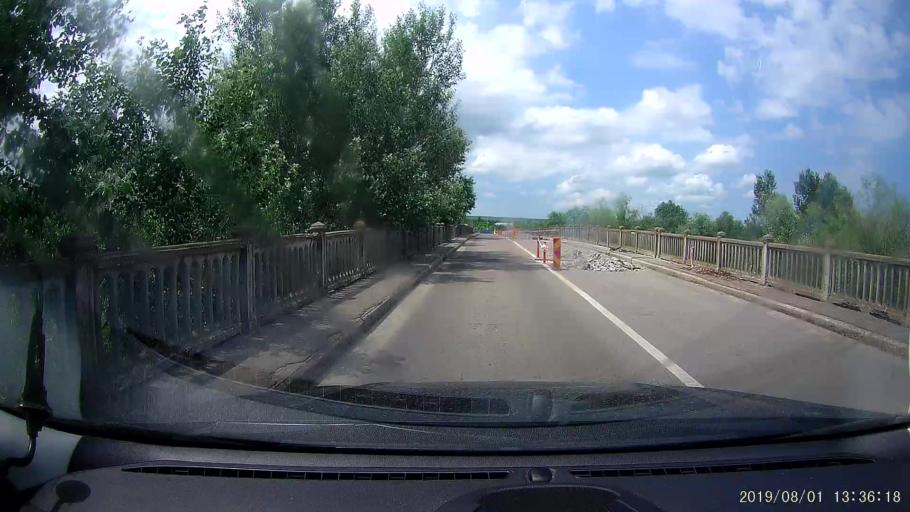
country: RO
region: Galati
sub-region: Comuna Oancea
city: Oancea
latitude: 45.9171
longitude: 28.1216
